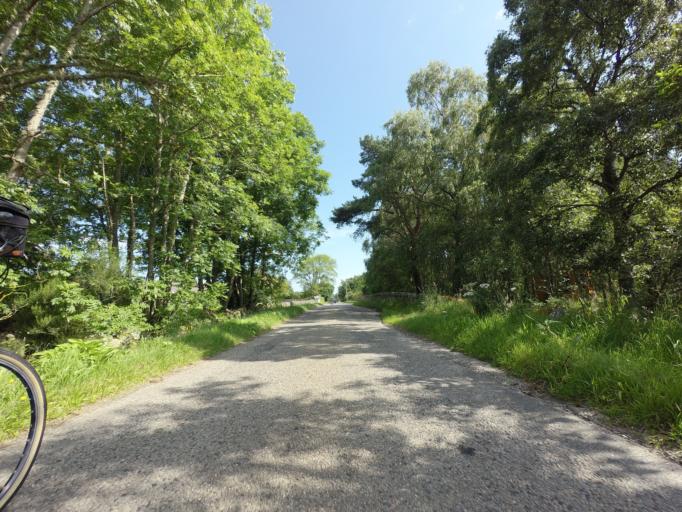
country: GB
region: Scotland
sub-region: Highland
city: Invergordon
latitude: 57.7271
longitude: -4.1956
